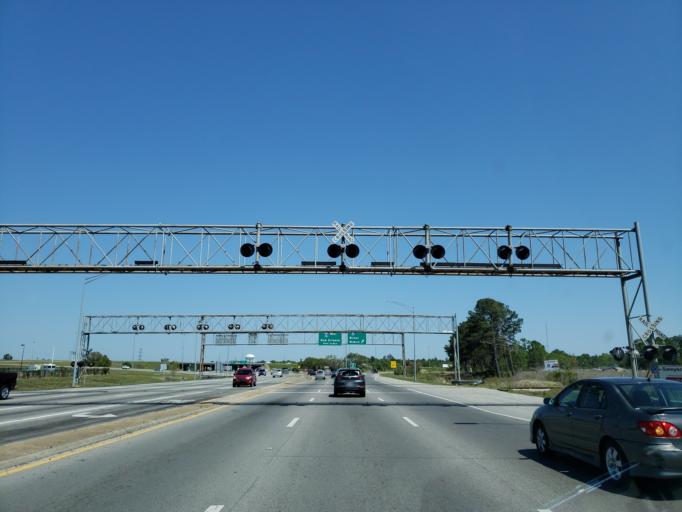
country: US
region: Mississippi
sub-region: Harrison County
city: West Gulfport
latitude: 30.4281
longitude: -89.0924
